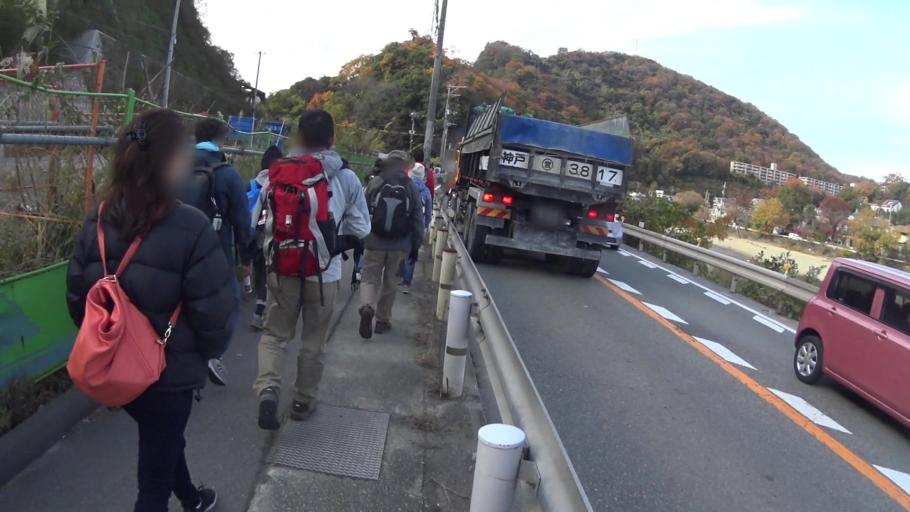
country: JP
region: Hyogo
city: Takarazuka
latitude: 34.8178
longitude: 135.3186
